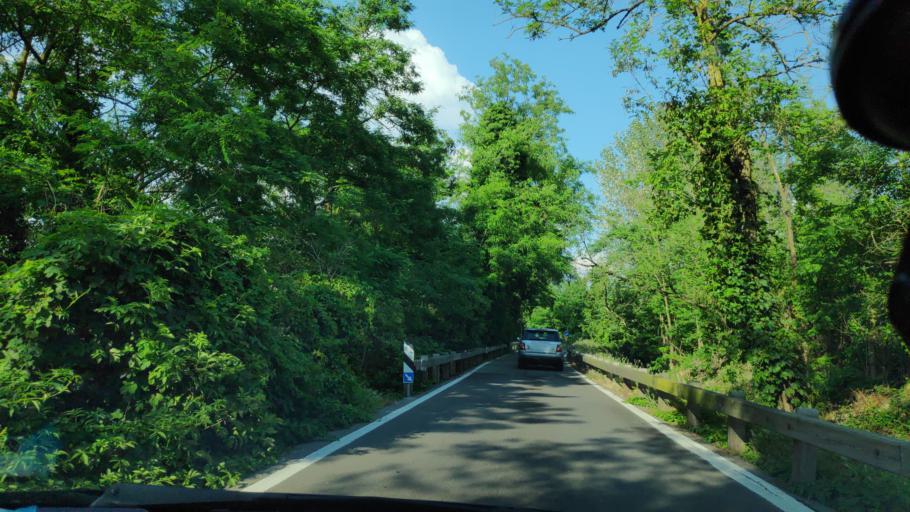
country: IT
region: Lombardy
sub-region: Citta metropolitana di Milano
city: Noverasco-Sporting Mirasole
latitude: 45.4069
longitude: 9.2171
